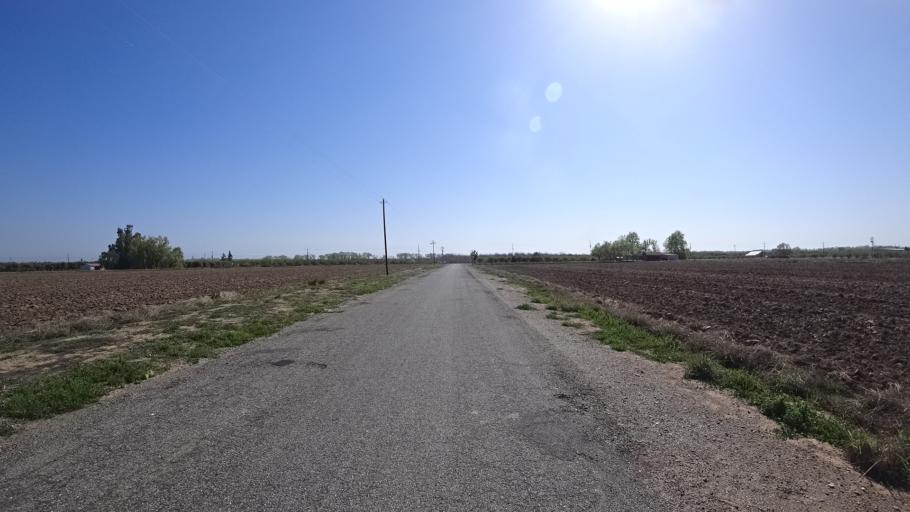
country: US
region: California
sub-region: Glenn County
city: Hamilton City
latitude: 39.6524
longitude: -122.0111
